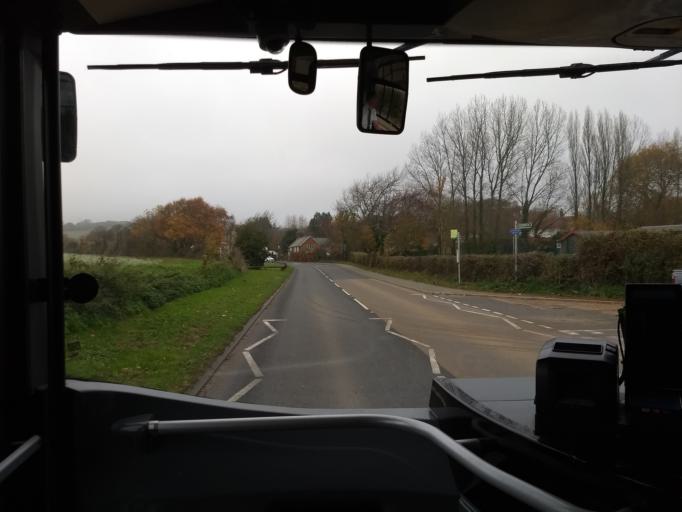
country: GB
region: England
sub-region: Isle of Wight
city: Newchurch
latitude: 50.6763
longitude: -1.2438
